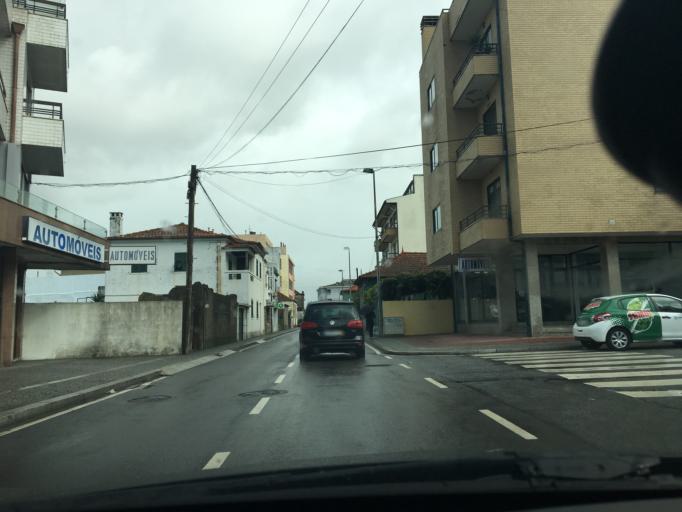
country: PT
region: Porto
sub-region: Matosinhos
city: Santa Cruz do Bispo
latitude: 41.2440
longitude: -8.6654
